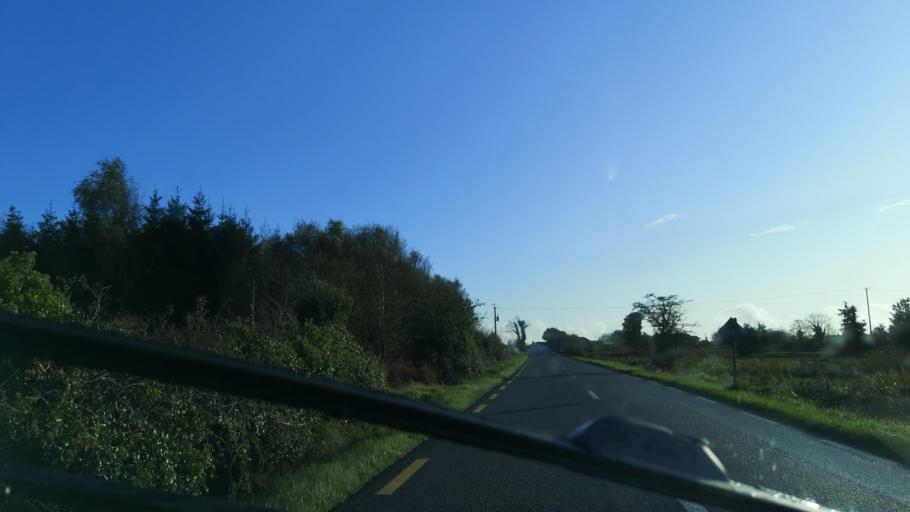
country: IE
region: Connaught
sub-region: Roscommon
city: Castlerea
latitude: 53.7904
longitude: -8.4898
